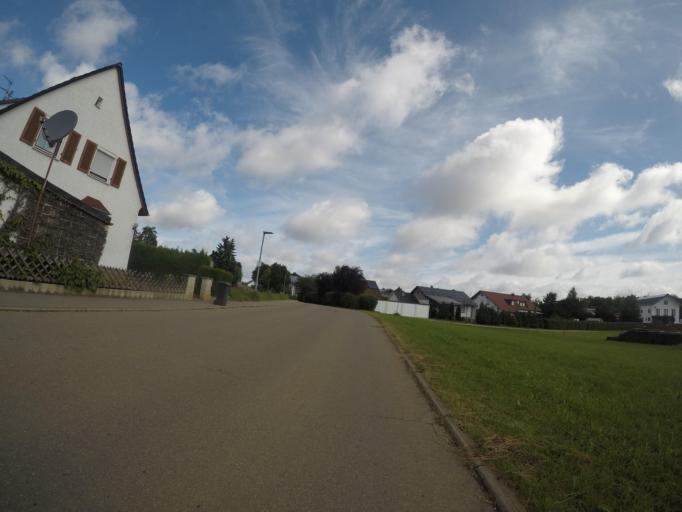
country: DE
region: Baden-Wuerttemberg
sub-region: Tuebingen Region
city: Laichingen
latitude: 48.4407
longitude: 9.6560
